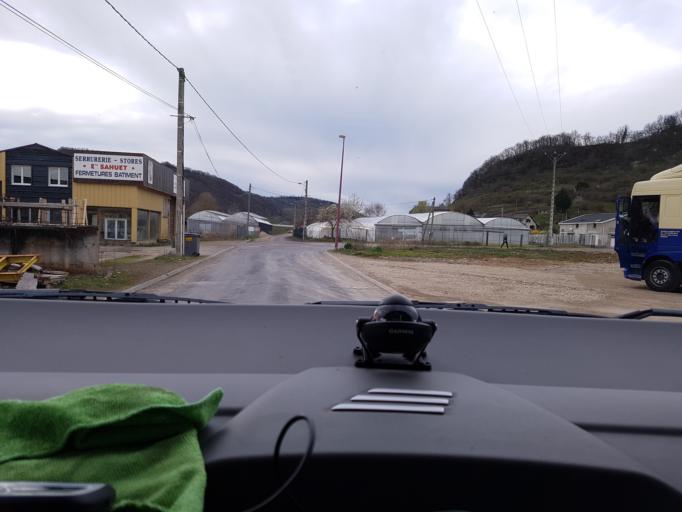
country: FR
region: Midi-Pyrenees
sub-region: Departement de l'Aveyron
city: Espalion
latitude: 44.5306
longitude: 2.7418
